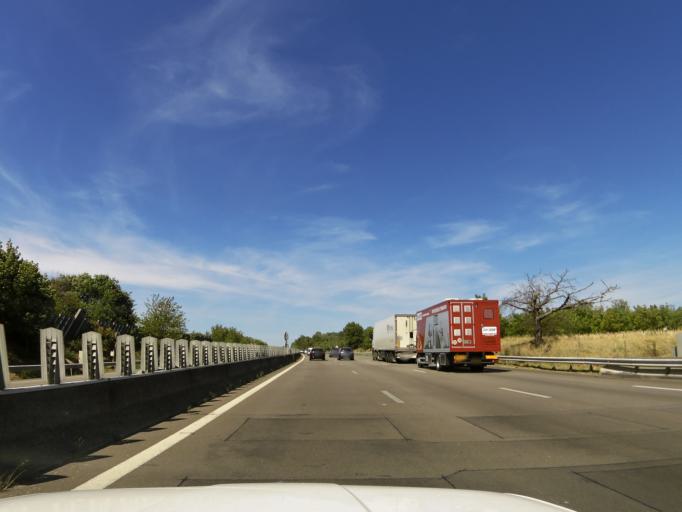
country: FR
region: Rhone-Alpes
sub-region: Departement de l'Isere
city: Roussillon
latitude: 45.3824
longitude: 4.8056
